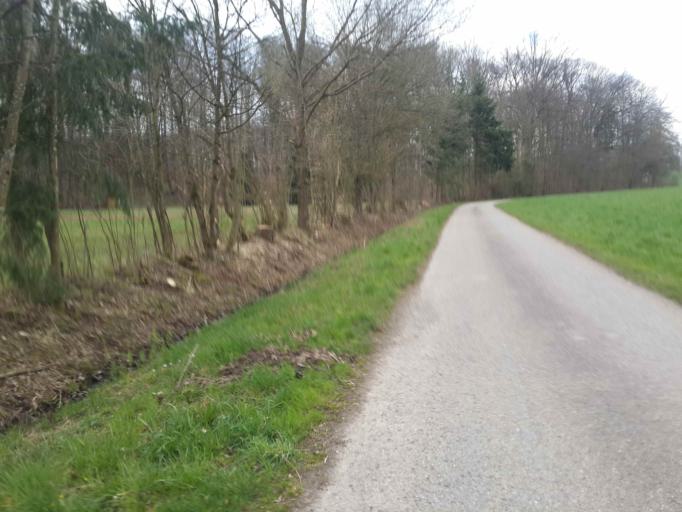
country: DE
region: Baden-Wuerttemberg
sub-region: Karlsruhe Region
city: Sinsheim
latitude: 49.2040
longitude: 8.8468
